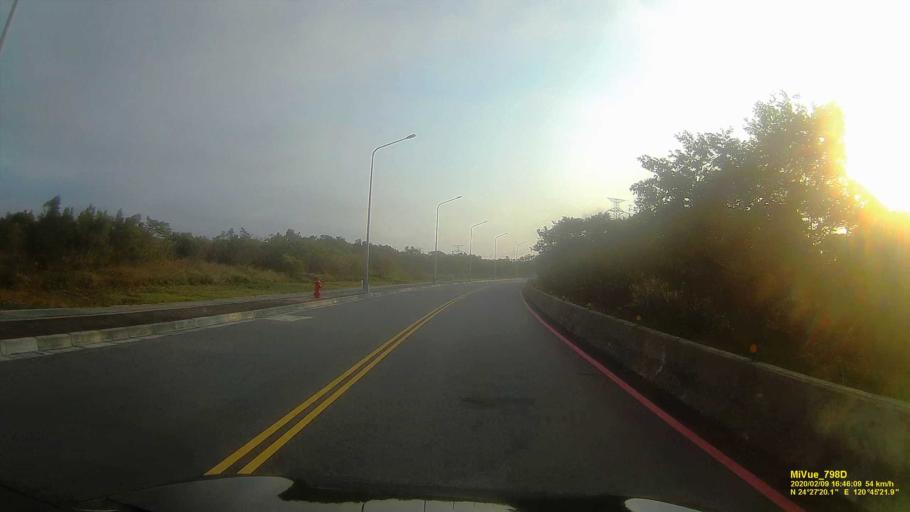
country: TW
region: Taiwan
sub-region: Miaoli
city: Miaoli
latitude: 24.4555
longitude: 120.7560
